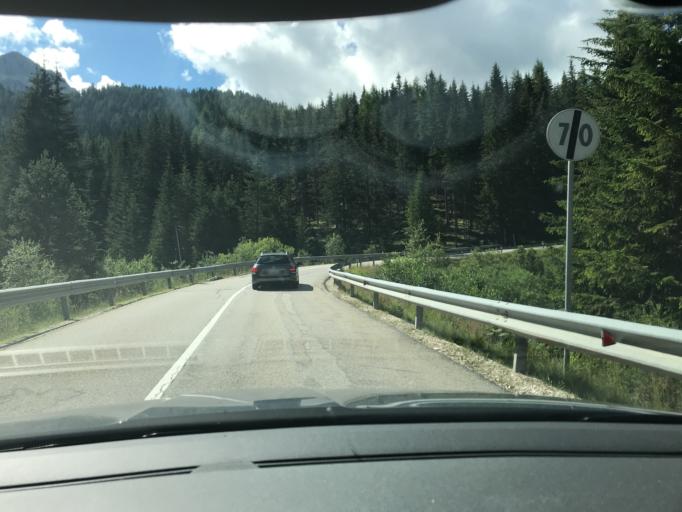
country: IT
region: Veneto
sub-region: Provincia di Belluno
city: Livinallongo del Col di Lana
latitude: 46.5527
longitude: 11.9688
